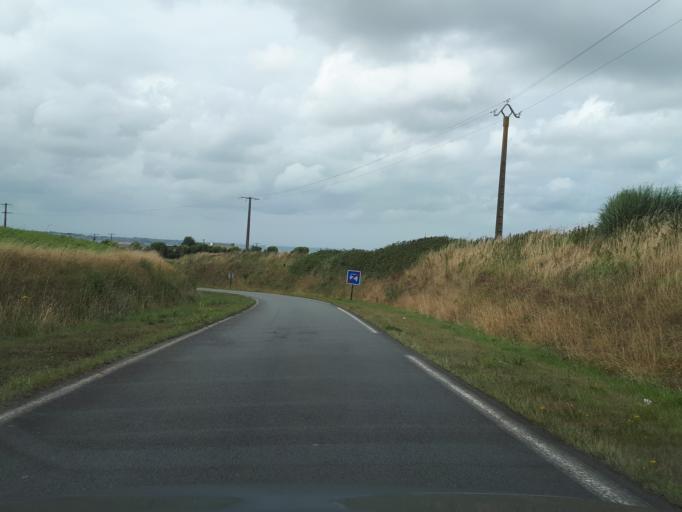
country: FR
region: Brittany
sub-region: Departement du Finistere
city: Henvic
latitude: 48.6357
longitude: -3.9237
